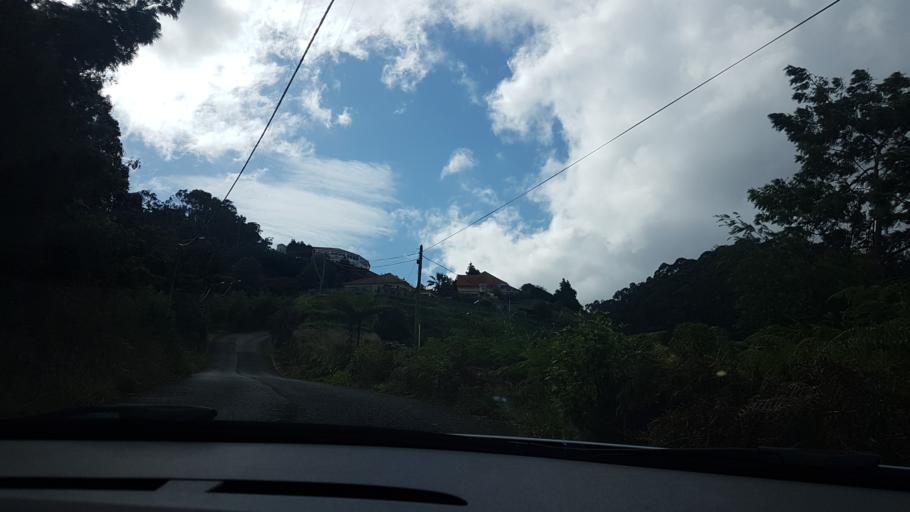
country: PT
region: Madeira
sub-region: Santa Cruz
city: Santa Cruz
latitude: 32.7312
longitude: -16.8227
